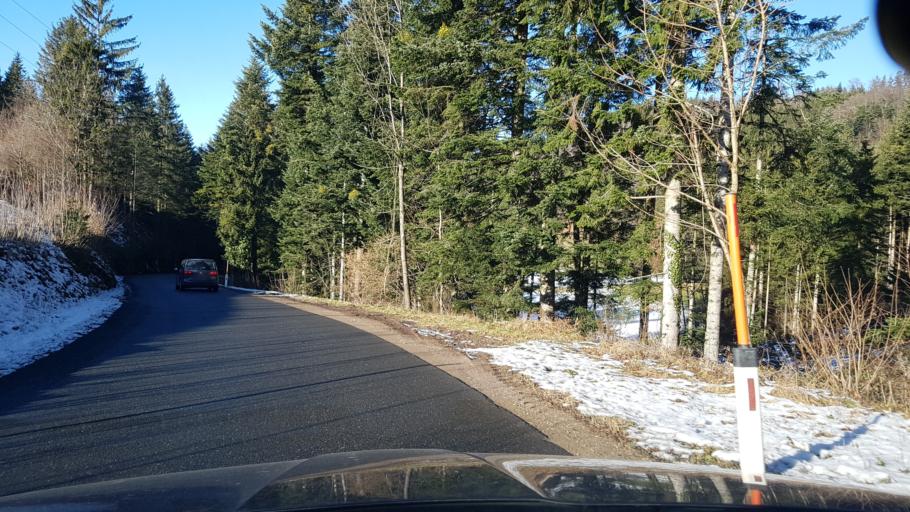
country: AT
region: Salzburg
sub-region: Politischer Bezirk Hallein
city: Golling an der Salzach
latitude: 47.6218
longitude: 13.1849
